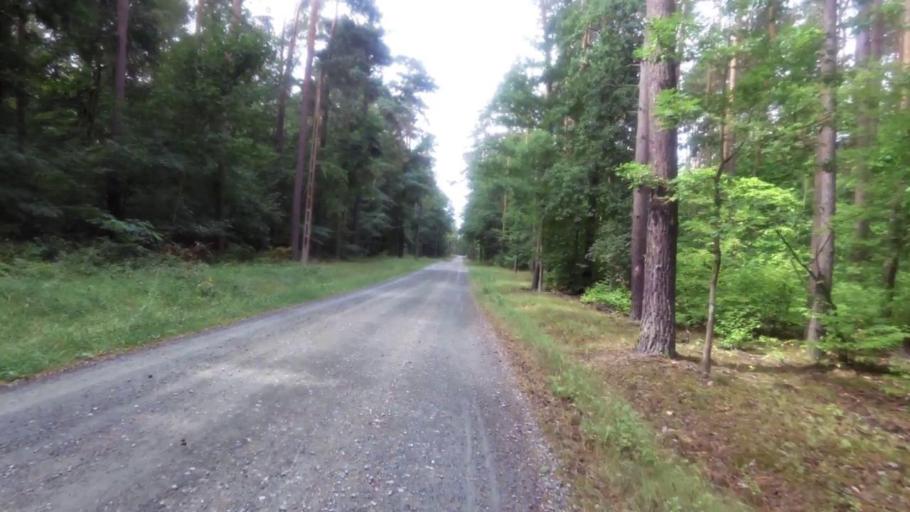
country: PL
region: West Pomeranian Voivodeship
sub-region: Powiat mysliborski
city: Debno
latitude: 52.7102
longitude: 14.6776
